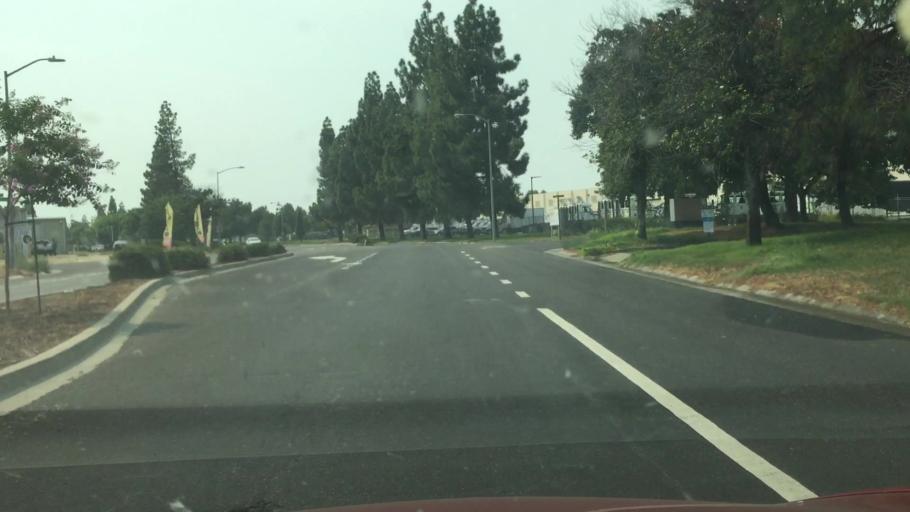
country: US
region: California
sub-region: San Joaquin County
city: Manteca
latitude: 37.7873
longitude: -121.2131
